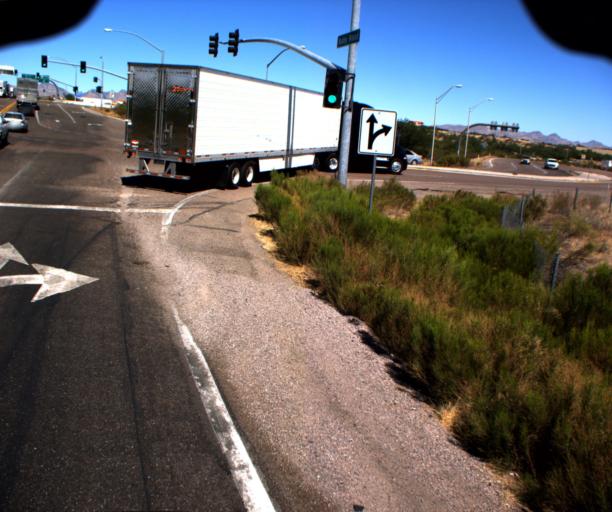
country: US
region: Arizona
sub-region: Santa Cruz County
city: Rio Rico
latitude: 31.4303
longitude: -110.9627
